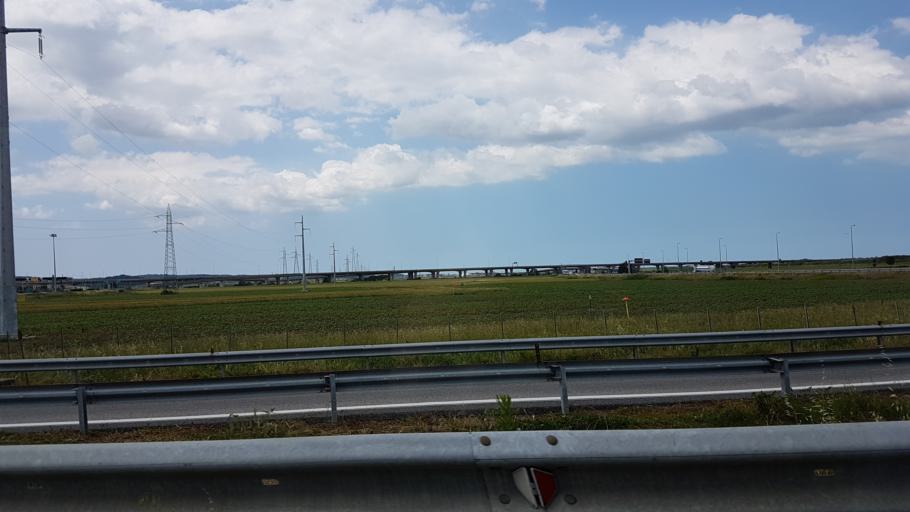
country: IT
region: Tuscany
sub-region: Provincia di Livorno
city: Vicarello
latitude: 43.6179
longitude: 10.4483
